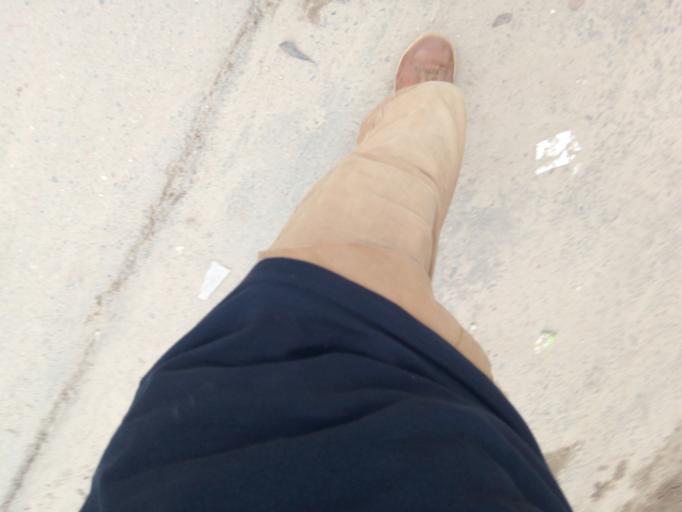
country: BD
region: Dhaka
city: Azimpur
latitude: 23.7118
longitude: 90.3633
